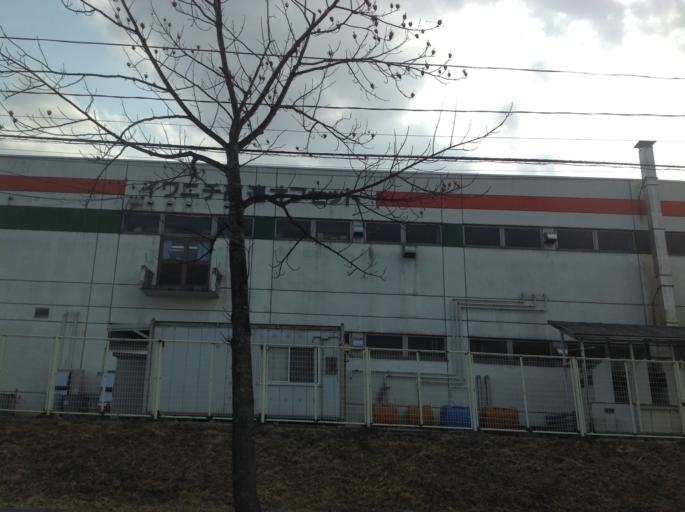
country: JP
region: Iwate
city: Ichinoseki
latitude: 38.9191
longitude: 141.1565
